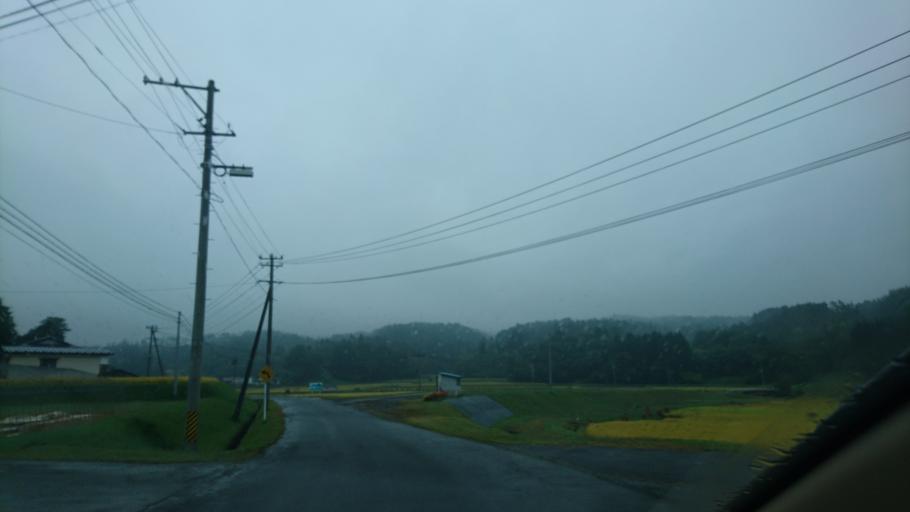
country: JP
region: Iwate
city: Mizusawa
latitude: 39.1232
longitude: 141.2059
